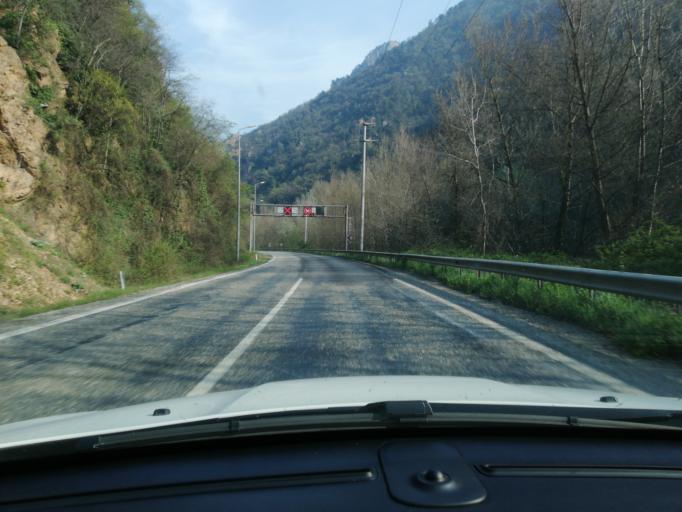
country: TR
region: Karabuk
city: Yenice
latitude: 41.1807
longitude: 32.4483
